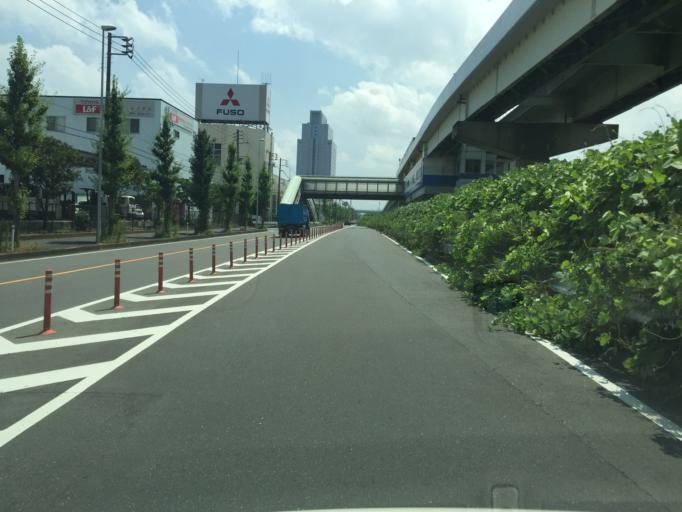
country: JP
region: Kanagawa
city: Yokosuka
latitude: 35.3593
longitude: 139.6438
